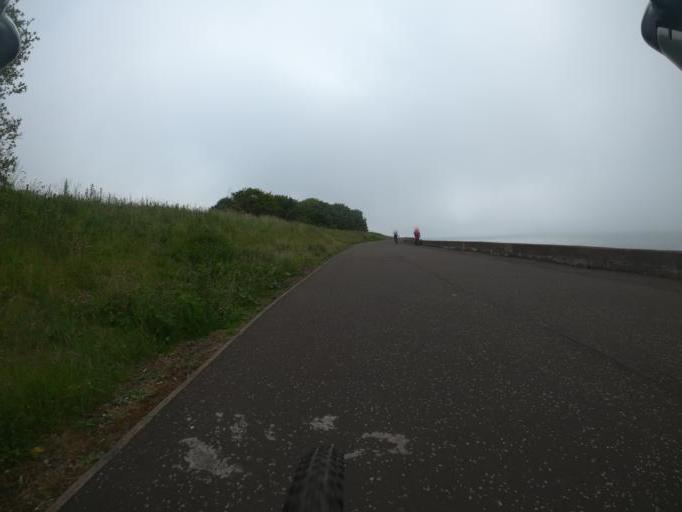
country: GB
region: Scotland
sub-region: Edinburgh
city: Edinburgh
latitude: 55.9836
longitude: -3.2471
